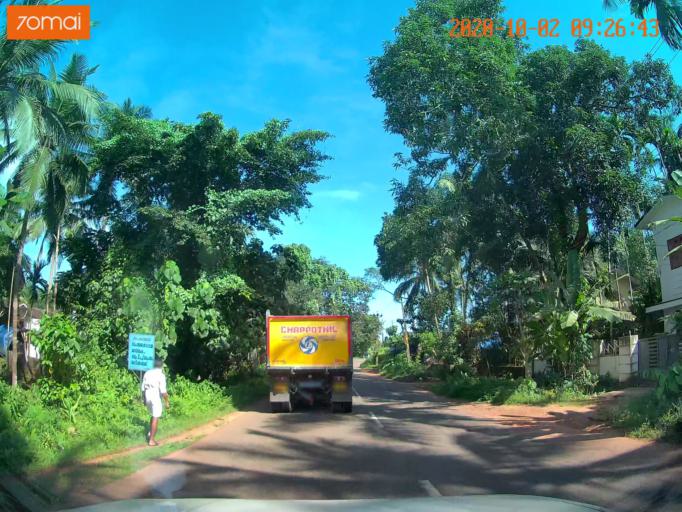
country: IN
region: Kerala
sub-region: Kozhikode
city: Naduvannur
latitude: 11.5941
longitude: 75.7659
